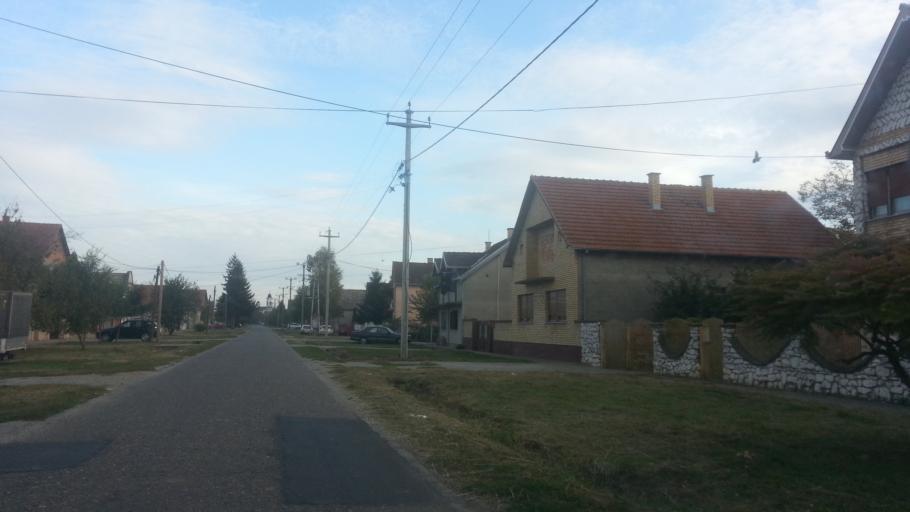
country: RS
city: Belegis
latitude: 45.0238
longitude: 20.3258
